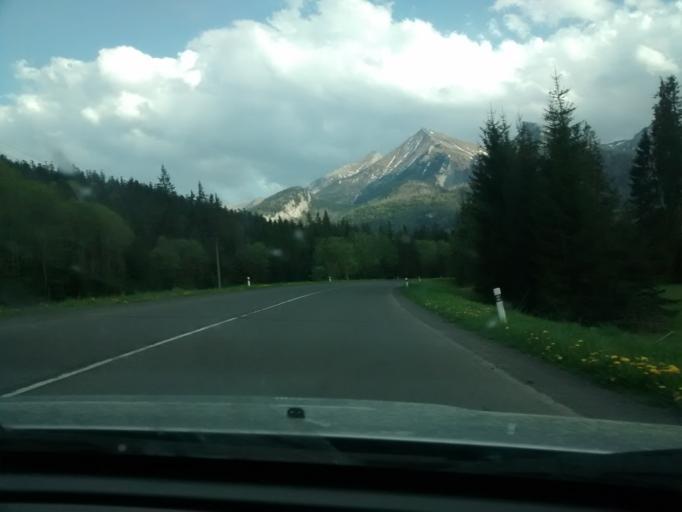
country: PL
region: Lesser Poland Voivodeship
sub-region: Powiat tatrzanski
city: Bukowina Tatrzanska
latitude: 49.2888
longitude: 20.1740
